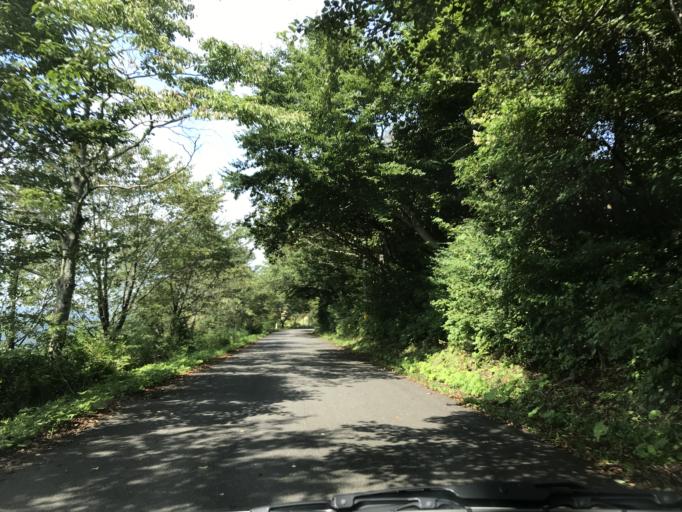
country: JP
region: Iwate
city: Ofunato
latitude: 38.9854
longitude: 141.4560
